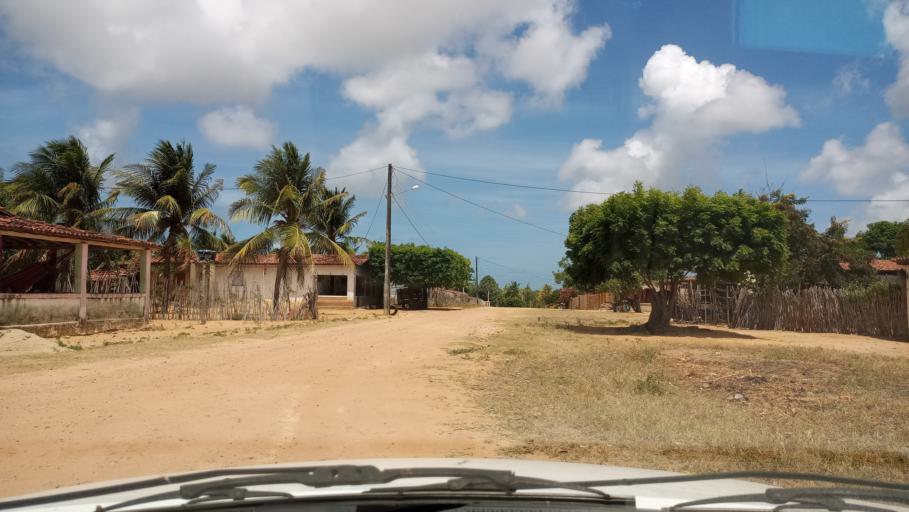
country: BR
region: Rio Grande do Norte
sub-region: Maxaranguape
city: Sao Miguel
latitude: -5.4810
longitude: -35.3303
